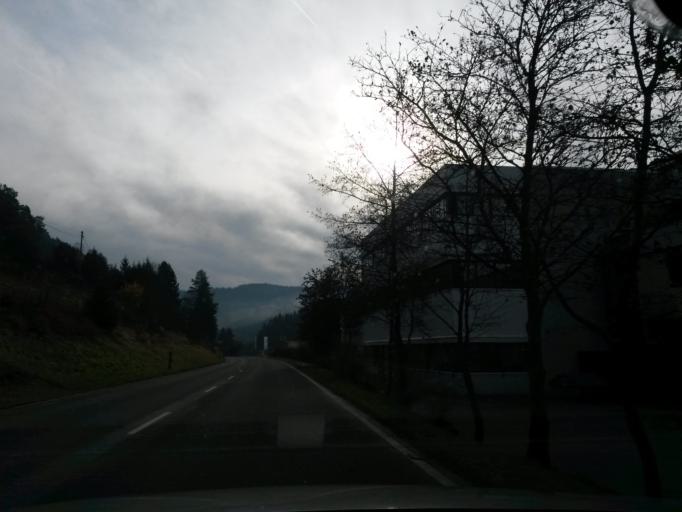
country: DE
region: Baden-Wuerttemberg
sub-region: Freiburg Region
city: Tennenbronn
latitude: 48.1894
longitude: 8.3652
